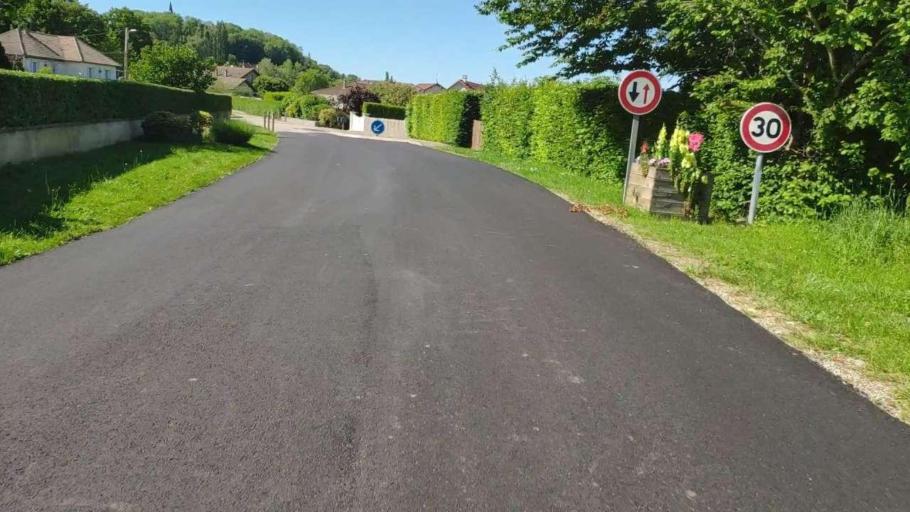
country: FR
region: Franche-Comte
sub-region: Departement du Jura
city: Perrigny
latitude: 46.7172
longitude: 5.5826
